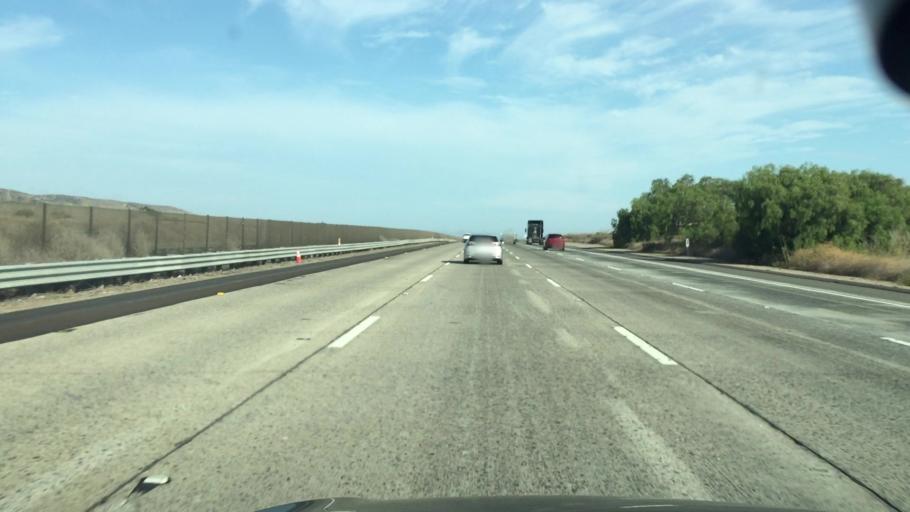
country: US
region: California
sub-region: Orange County
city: San Clemente
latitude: 33.3333
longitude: -117.4992
